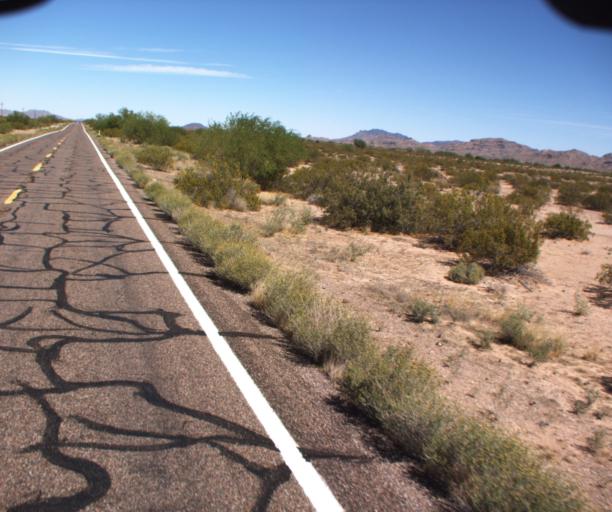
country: US
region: Arizona
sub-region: Pima County
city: Ajo
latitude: 32.6376
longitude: -112.8636
